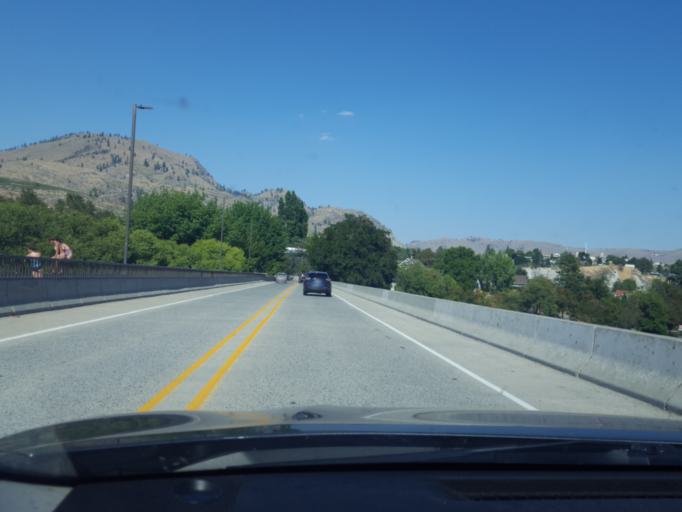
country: US
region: Washington
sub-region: Chelan County
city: Chelan
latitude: 47.8359
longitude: -120.0171
